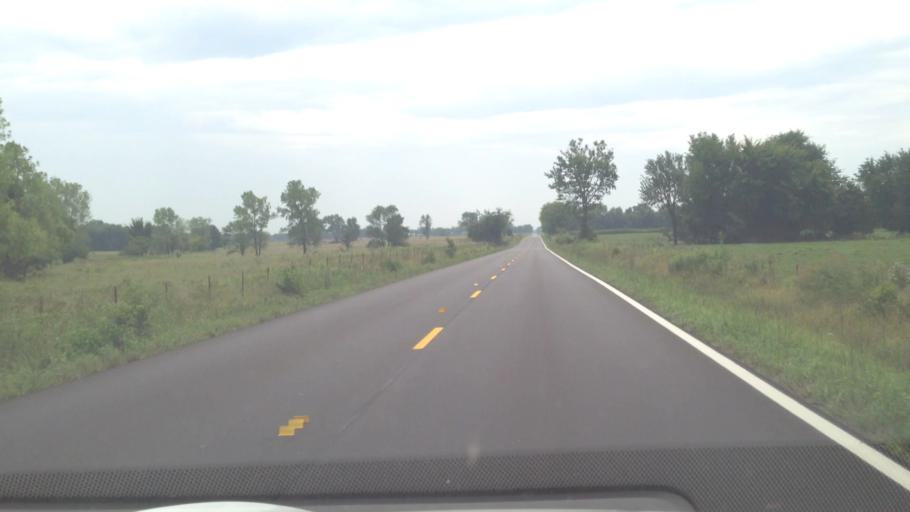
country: US
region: Kansas
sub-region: Crawford County
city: Girard
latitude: 37.5415
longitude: -94.9605
